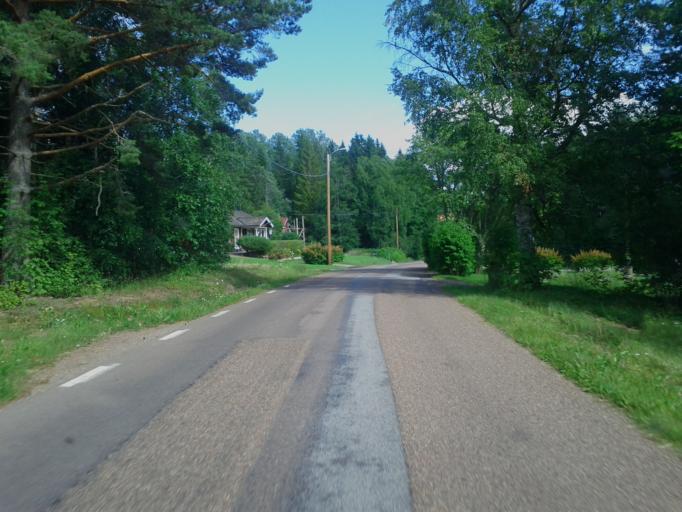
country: SE
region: Dalarna
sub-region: Rattviks Kommun
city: Raettvik
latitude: 60.9175
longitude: 15.0846
